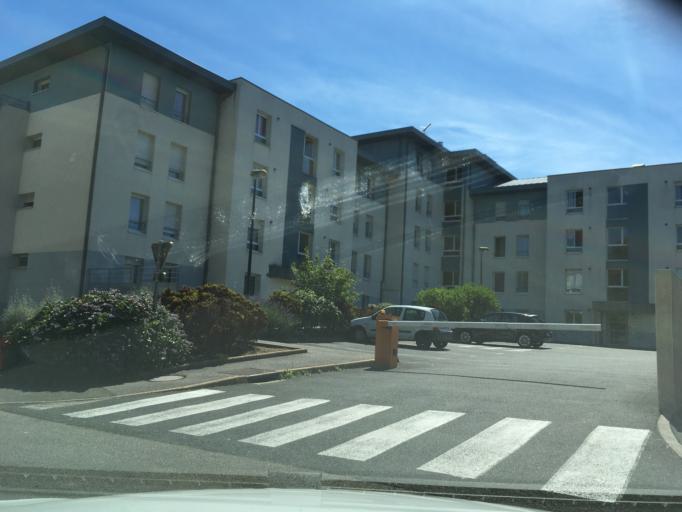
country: FR
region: Brittany
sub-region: Departement du Finistere
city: Quimper
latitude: 47.9870
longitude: -4.1257
